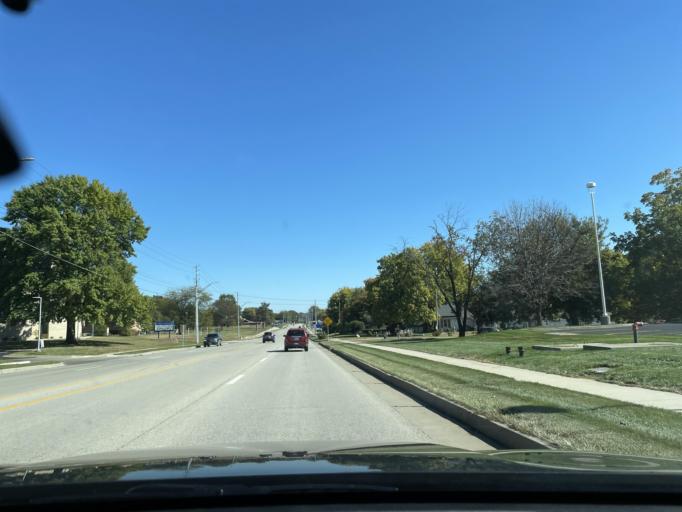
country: US
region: Missouri
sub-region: Buchanan County
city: Saint Joseph
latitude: 39.7790
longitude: -94.7844
